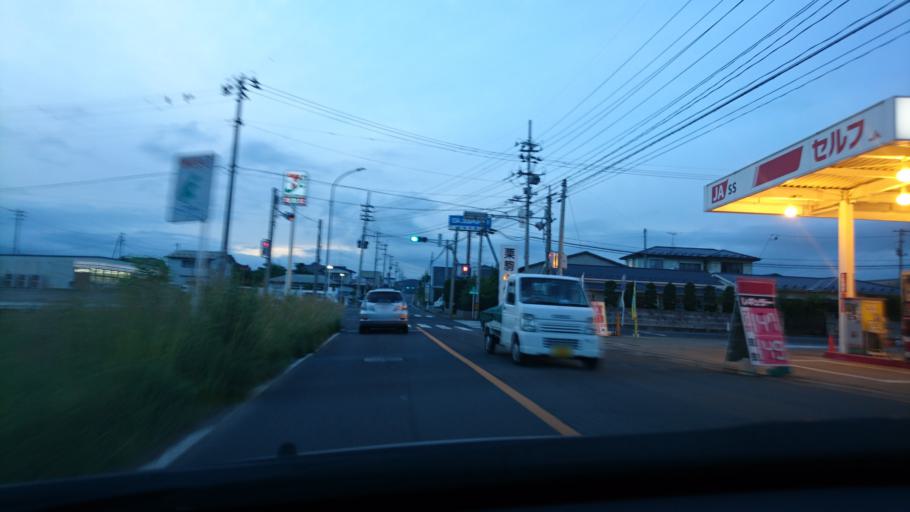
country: JP
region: Iwate
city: Ichinoseki
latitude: 38.8162
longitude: 140.9859
